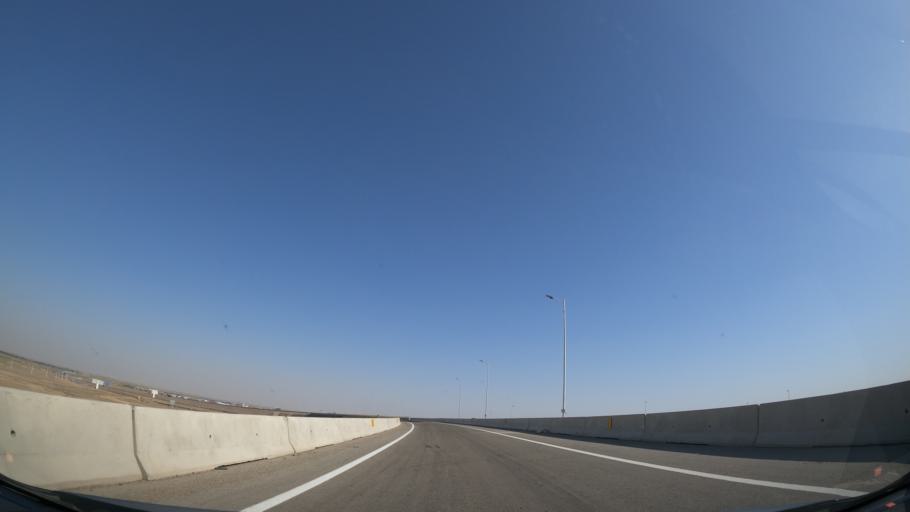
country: IR
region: Tehran
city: Eqbaliyeh
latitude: 35.1333
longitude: 51.5110
